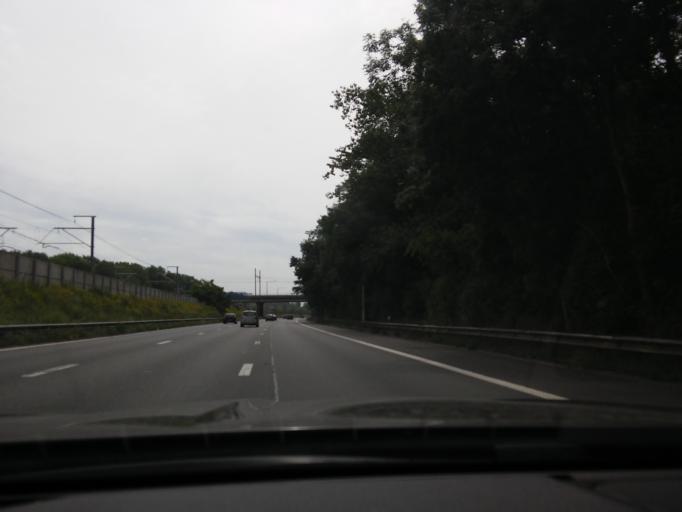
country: BE
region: Flanders
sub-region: Provincie Vlaams-Brabant
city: Zemst
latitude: 50.9845
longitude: 4.4813
